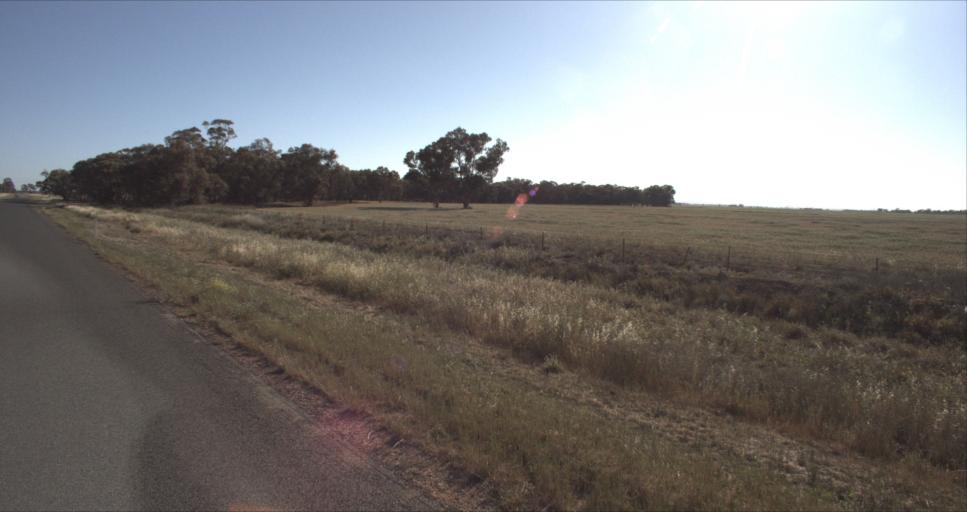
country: AU
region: New South Wales
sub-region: Leeton
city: Leeton
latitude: -34.5651
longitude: 146.2646
